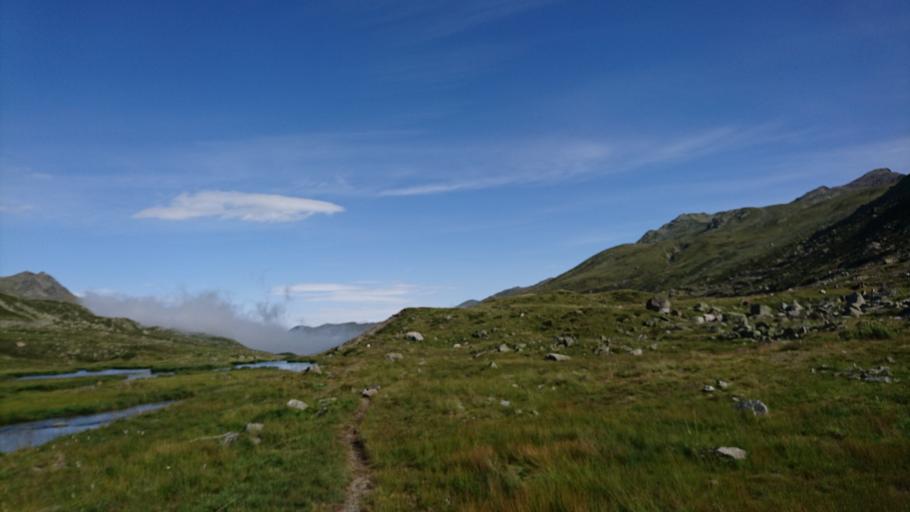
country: CH
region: Grisons
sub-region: Praettigau/Davos District
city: Davos
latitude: 46.7623
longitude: 9.9440
